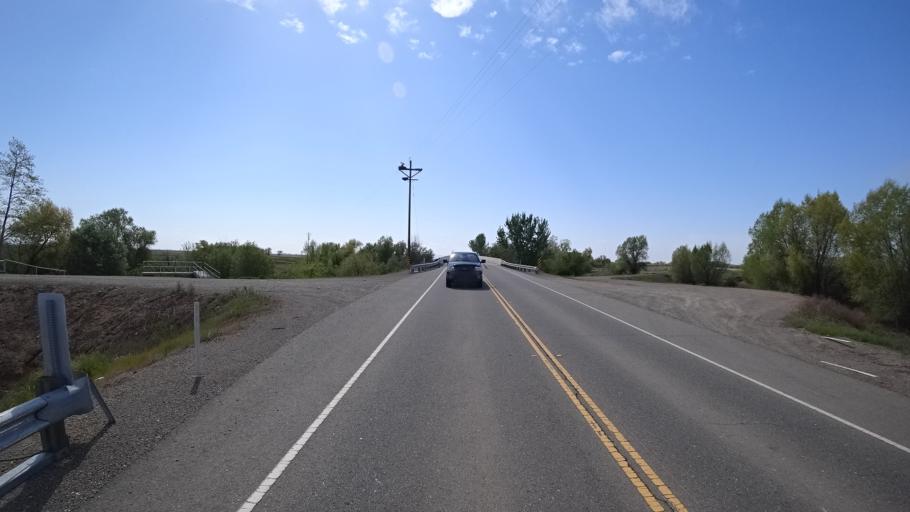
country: US
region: California
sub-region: Butte County
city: Durham
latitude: 39.5349
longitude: -121.8565
